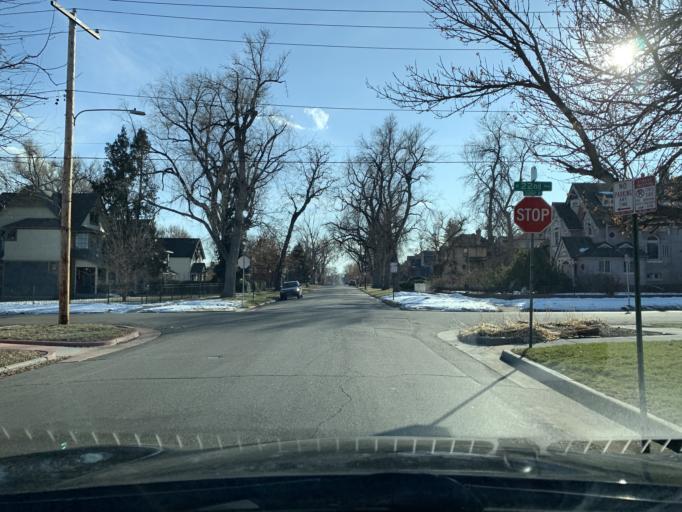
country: US
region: Colorado
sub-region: Jefferson County
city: Edgewater
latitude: 39.7503
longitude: -105.0269
